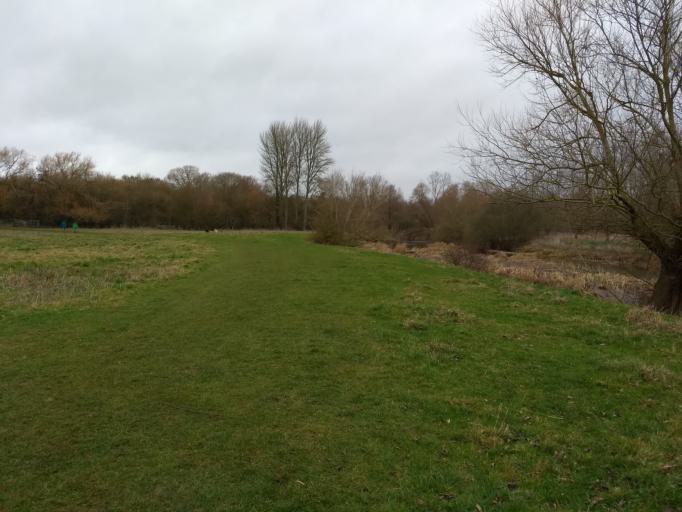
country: GB
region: England
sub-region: Bedford
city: Odell
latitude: 52.2049
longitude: -0.5894
